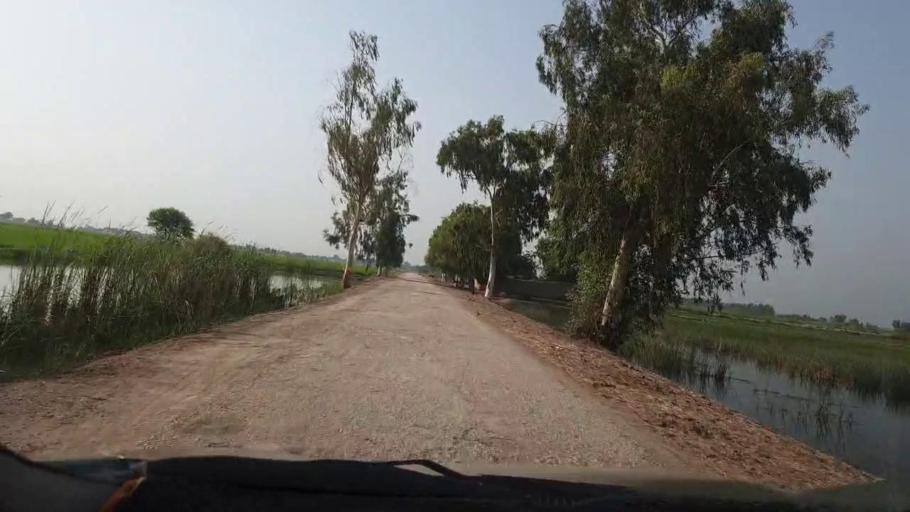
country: PK
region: Sindh
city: Goth Garelo
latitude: 27.4743
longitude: 68.0872
